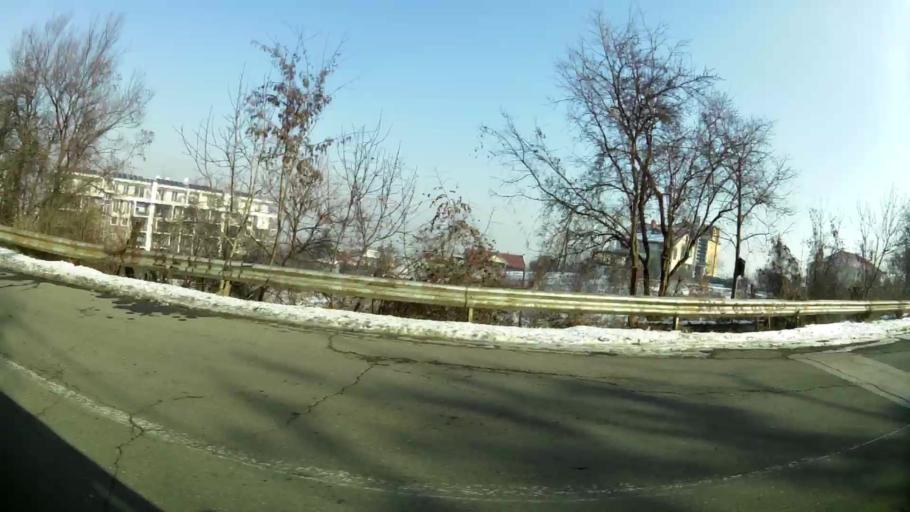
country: MK
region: Karpos
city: Skopje
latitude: 41.9802
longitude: 21.4239
